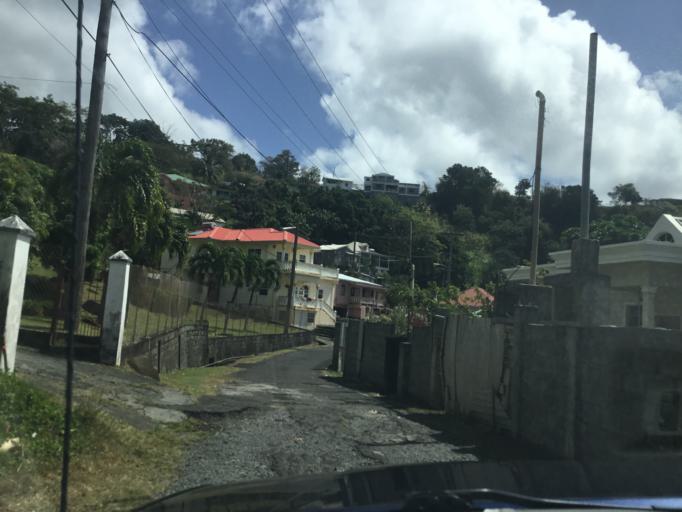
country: VC
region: Saint George
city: Kingstown Park
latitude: 13.1599
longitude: -61.2353
